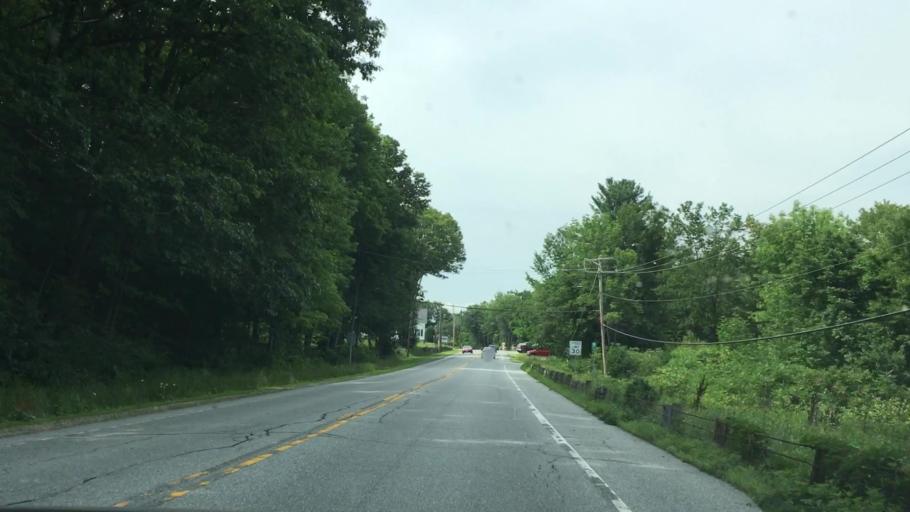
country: US
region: New Hampshire
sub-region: Hillsborough County
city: Antrim
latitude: 43.0224
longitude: -71.9355
